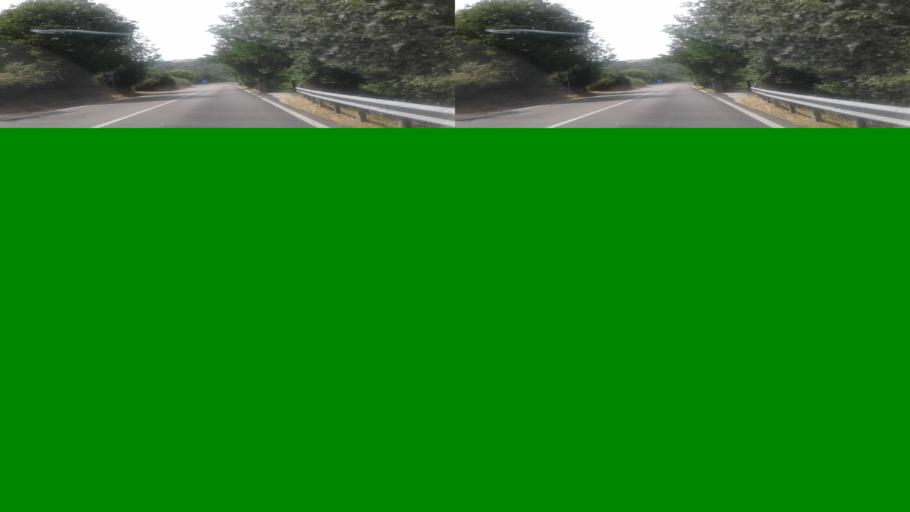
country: IT
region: Sardinia
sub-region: Provincia di Olbia-Tempio
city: Tempio Pausania
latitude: 40.9075
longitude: 9.0897
